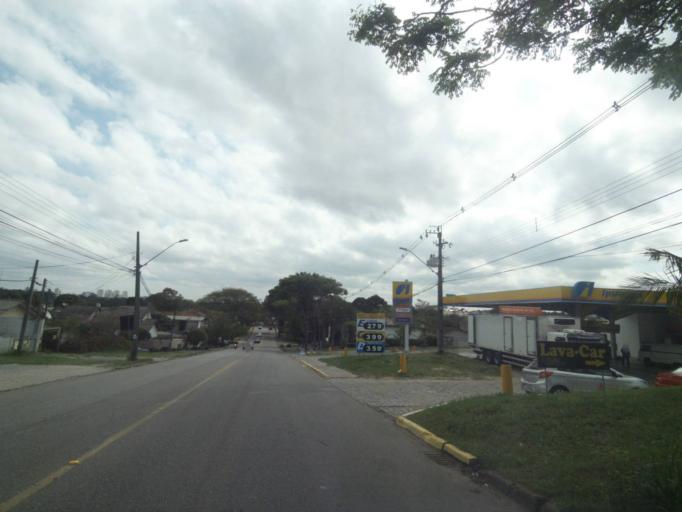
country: BR
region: Parana
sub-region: Pinhais
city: Pinhais
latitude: -25.4159
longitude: -49.2157
